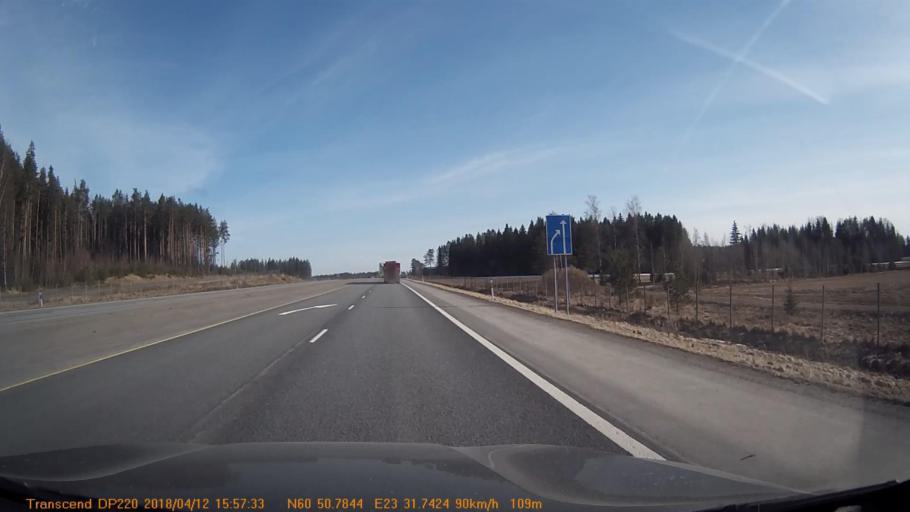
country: FI
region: Haeme
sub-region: Forssa
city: Jokioinen
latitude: 60.8463
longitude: 23.5292
